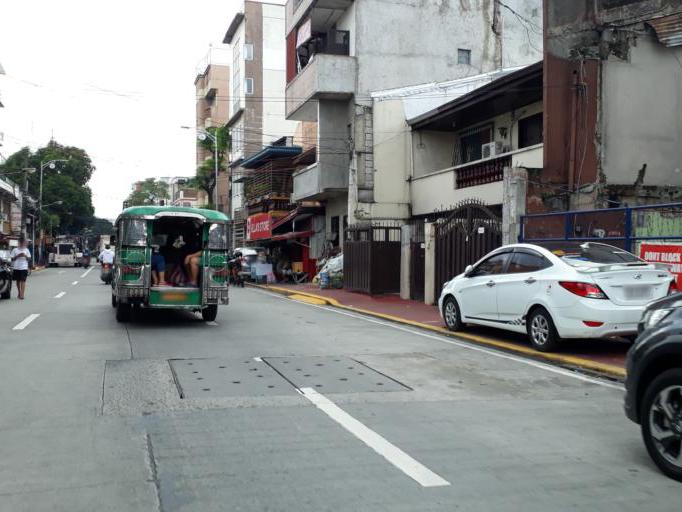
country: PH
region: Metro Manila
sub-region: City of Manila
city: Manila
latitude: 14.6135
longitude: 120.9935
